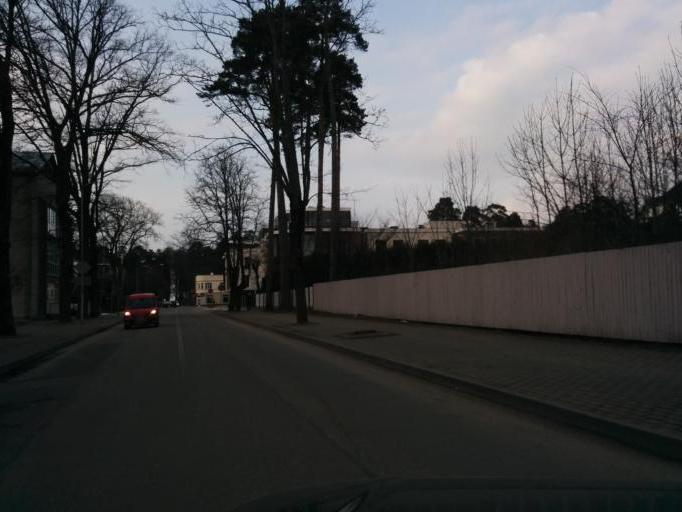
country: LV
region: Babite
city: Pinki
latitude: 56.9835
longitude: 23.8559
